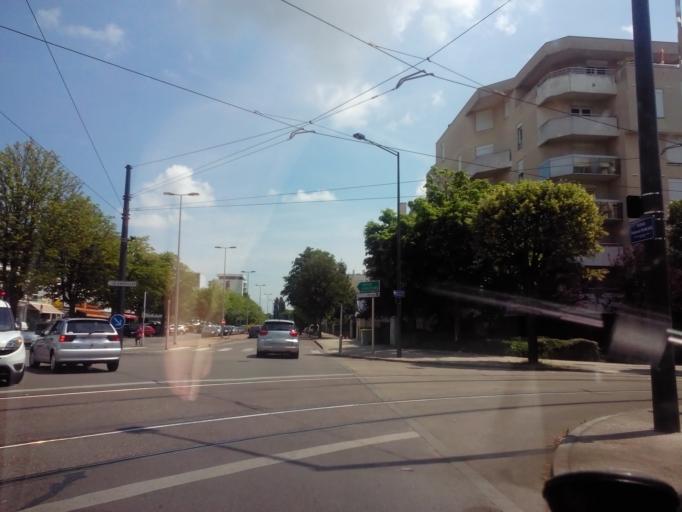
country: FR
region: Bourgogne
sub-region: Departement de la Cote-d'Or
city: Saint-Apollinaire
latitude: 47.3288
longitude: 5.0648
